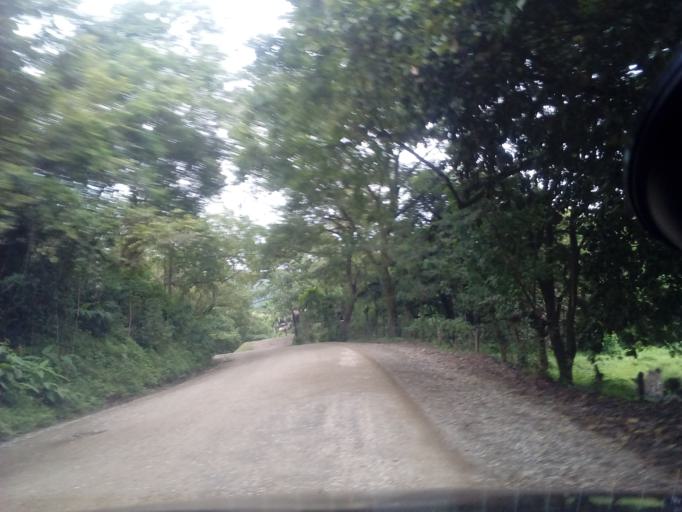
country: CR
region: Guanacaste
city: Samara
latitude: 9.9203
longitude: -85.5697
